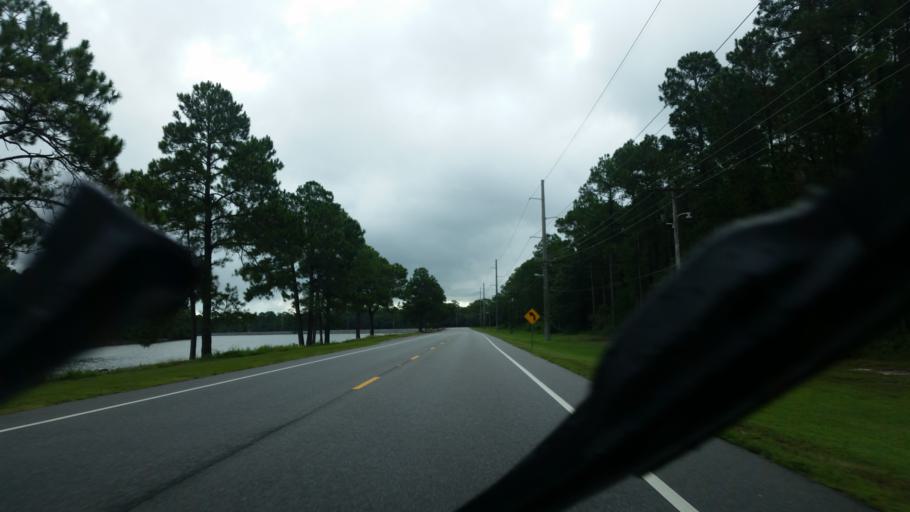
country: US
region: Alabama
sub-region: Baldwin County
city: Gulf Shores
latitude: 30.2794
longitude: -87.6575
